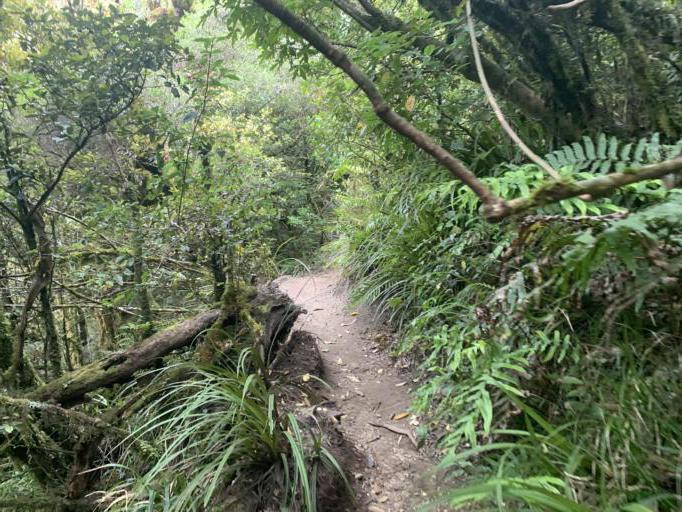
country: NZ
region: Waikato
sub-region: Taupo District
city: Taupo
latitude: -38.6953
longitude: 176.1615
